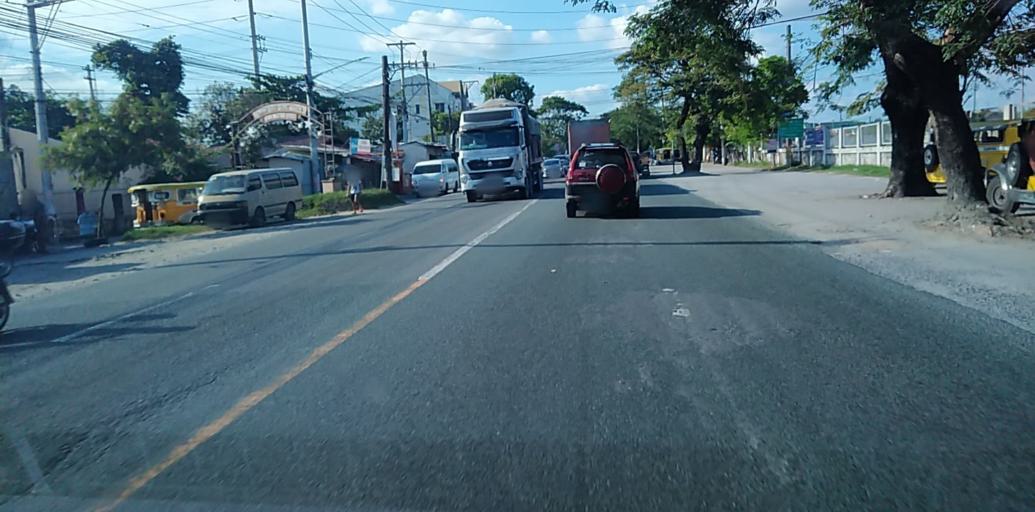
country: PH
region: Central Luzon
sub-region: Province of Pampanga
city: Telabastagan
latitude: 15.1137
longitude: 120.6094
